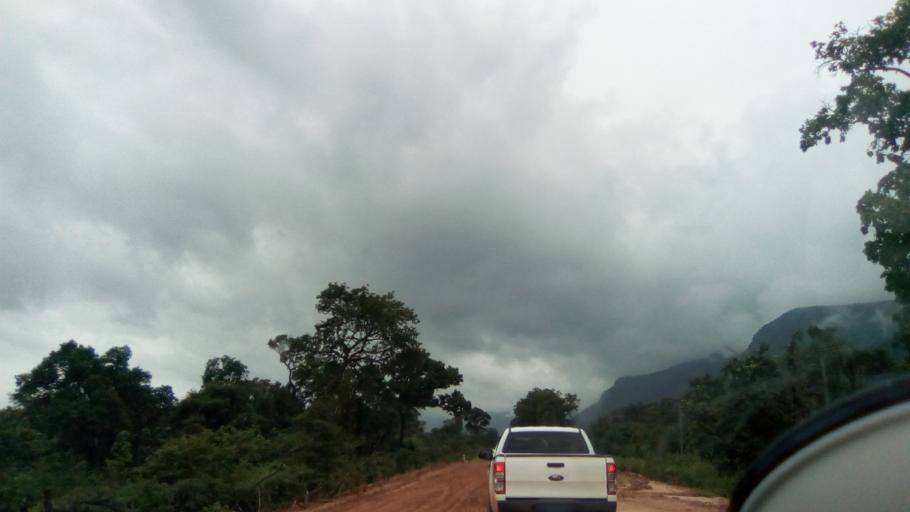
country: LA
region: Attapu
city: Attapu
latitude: 14.7676
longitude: 106.7313
